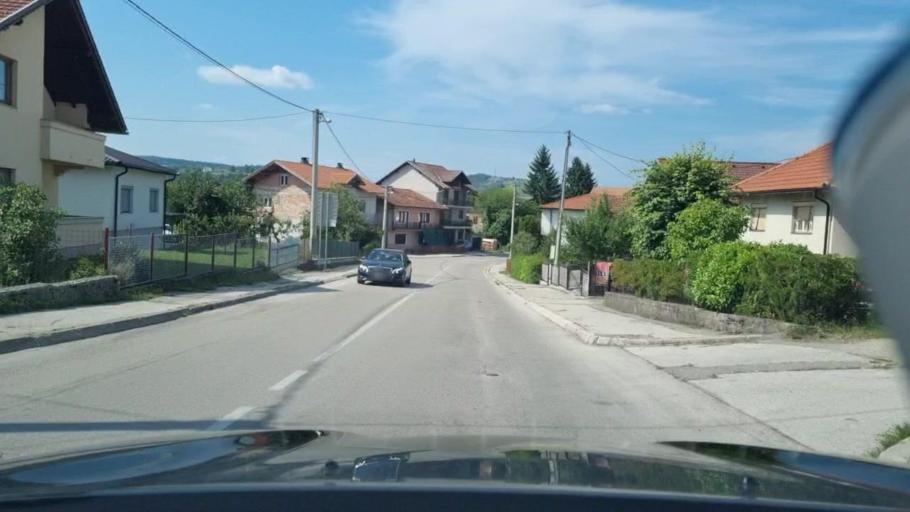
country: BA
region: Federation of Bosnia and Herzegovina
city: Bosanska Krupa
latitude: 44.8785
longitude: 16.1565
